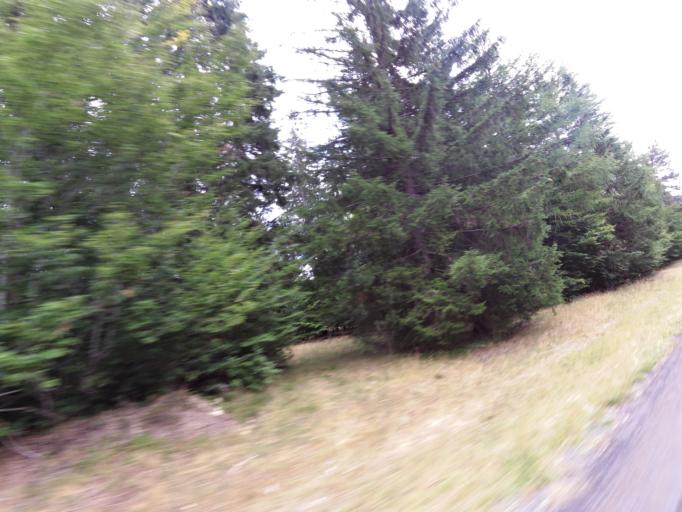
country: FR
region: Languedoc-Roussillon
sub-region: Departement du Gard
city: Valleraugue
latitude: 44.0847
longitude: 3.5627
